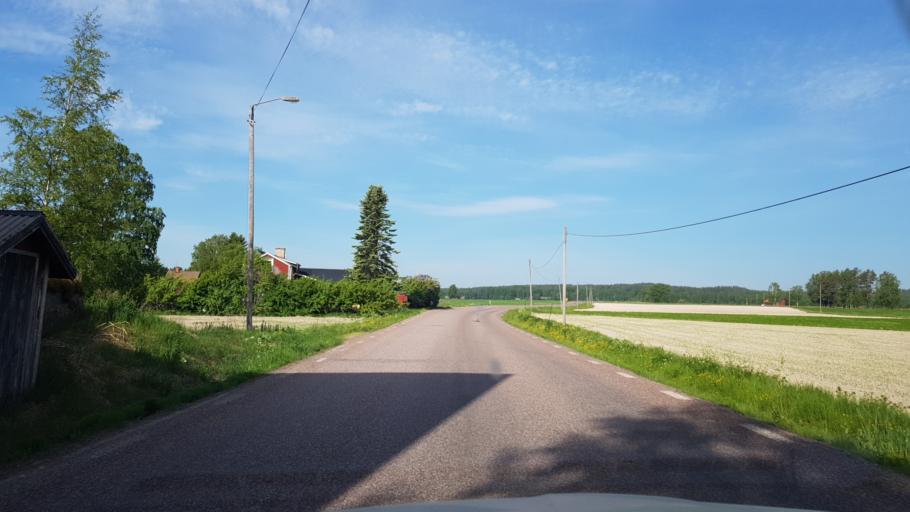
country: SE
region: Dalarna
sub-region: Saters Kommun
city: Saeter
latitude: 60.4153
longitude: 15.7259
